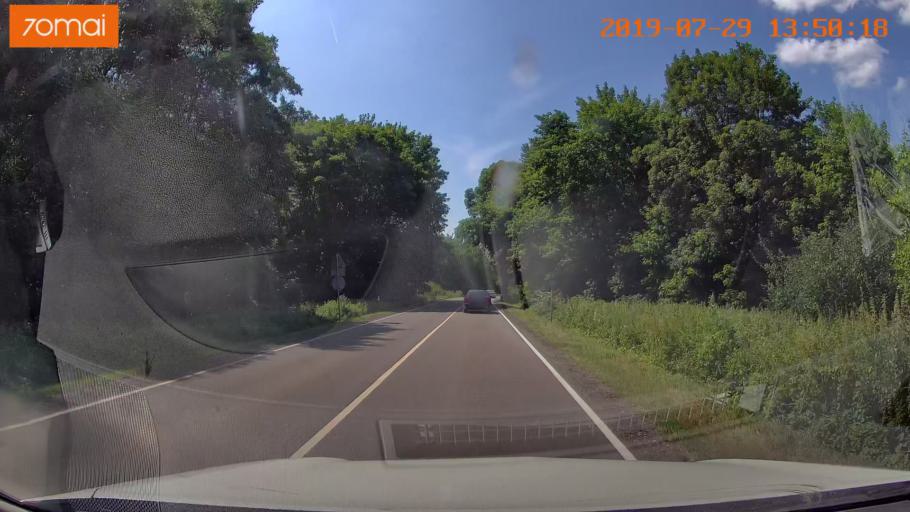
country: RU
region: Kaliningrad
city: Primorsk
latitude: 54.7297
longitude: 20.0159
